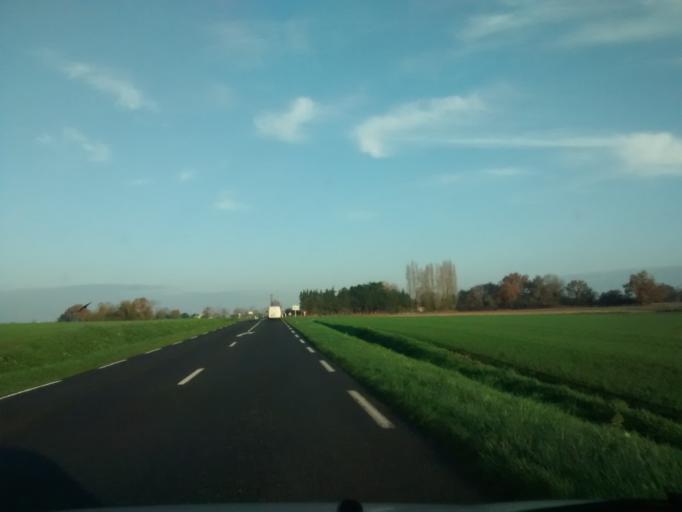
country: FR
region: Lower Normandy
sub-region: Departement de la Manche
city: Pontorson
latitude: 48.5334
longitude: -1.4881
